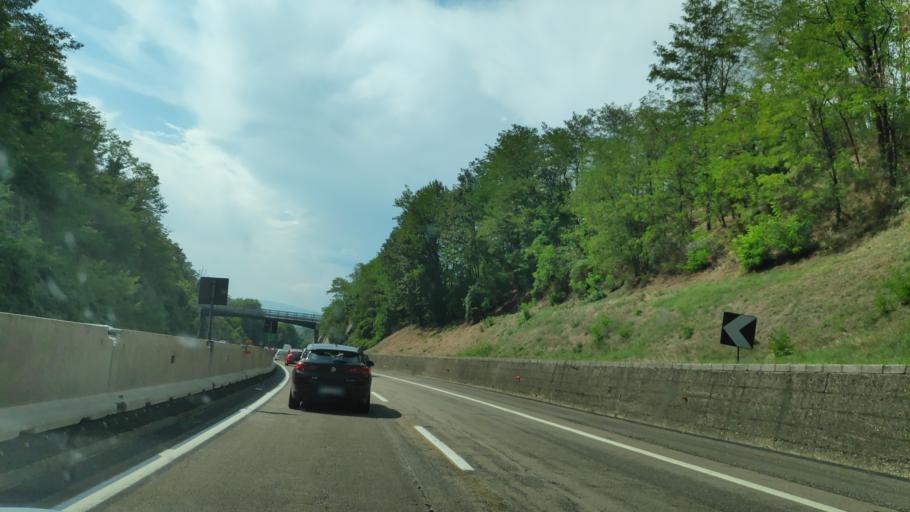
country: IT
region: Tuscany
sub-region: Province of Arezzo
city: Montalto
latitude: 43.5129
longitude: 11.6425
